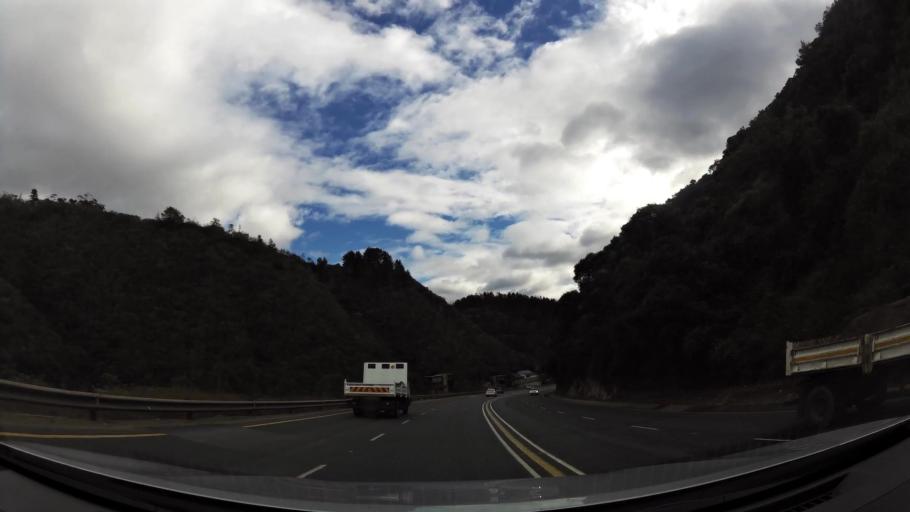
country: ZA
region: Western Cape
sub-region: Eden District Municipality
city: George
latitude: -33.9944
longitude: 22.5533
